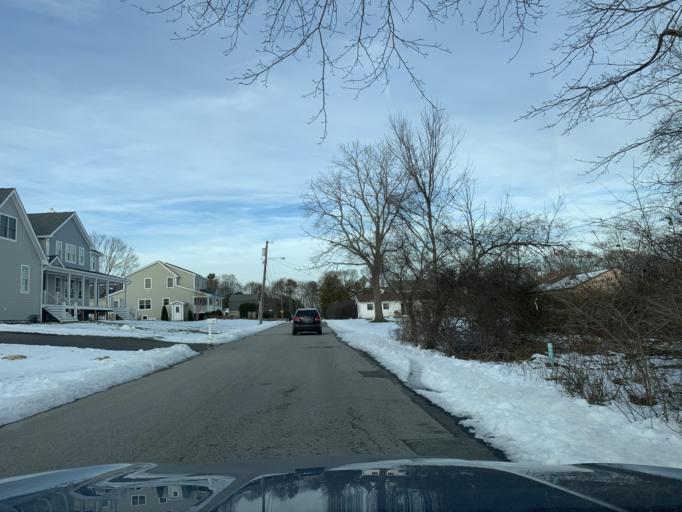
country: US
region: Rhode Island
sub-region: Washington County
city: North Kingstown
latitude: 41.5840
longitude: -71.4344
